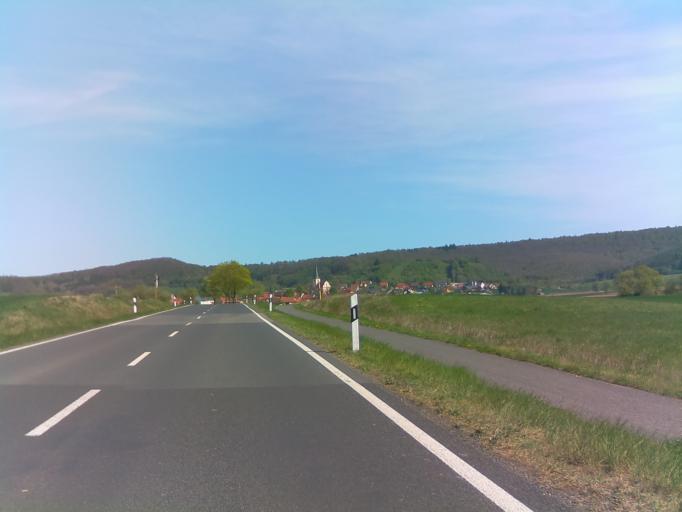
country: DE
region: Bavaria
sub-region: Regierungsbezirk Unterfranken
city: Hofheim in Unterfranken
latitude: 50.1387
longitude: 10.5417
